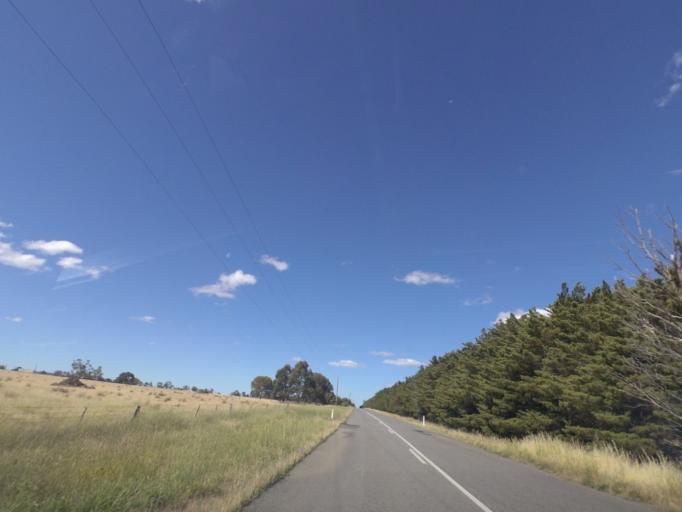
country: AU
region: Victoria
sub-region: Hume
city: Sunbury
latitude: -37.4389
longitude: 144.8357
